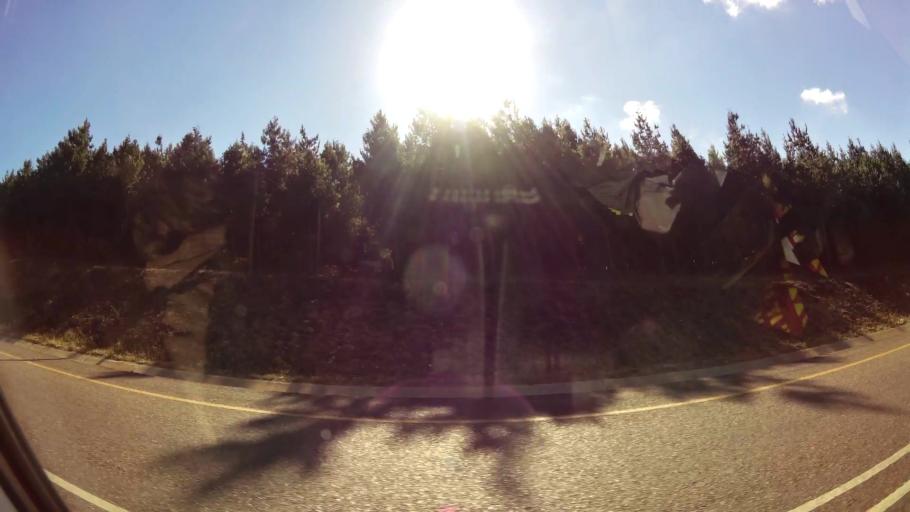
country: ZA
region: Limpopo
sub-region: Capricorn District Municipality
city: Mankoeng
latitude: -23.9125
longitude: 29.9646
